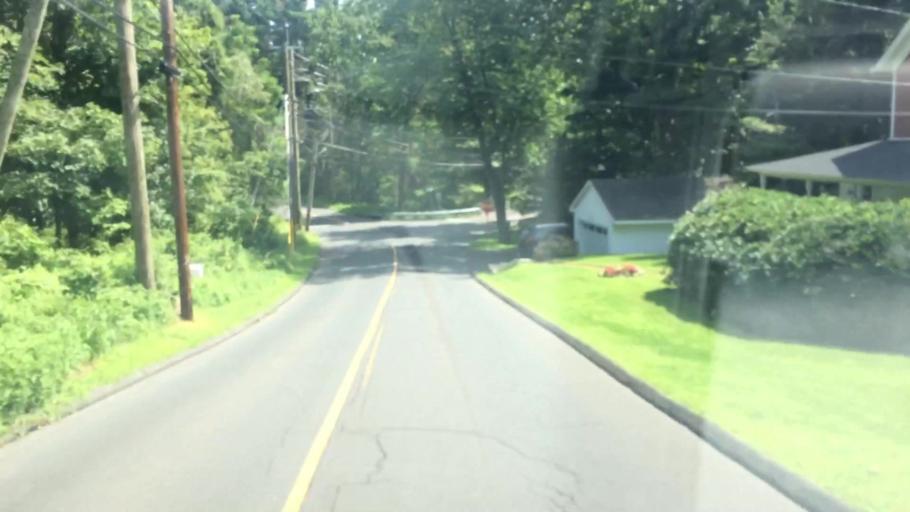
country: US
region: Connecticut
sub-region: Fairfield County
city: Danbury
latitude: 41.4054
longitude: -73.4941
